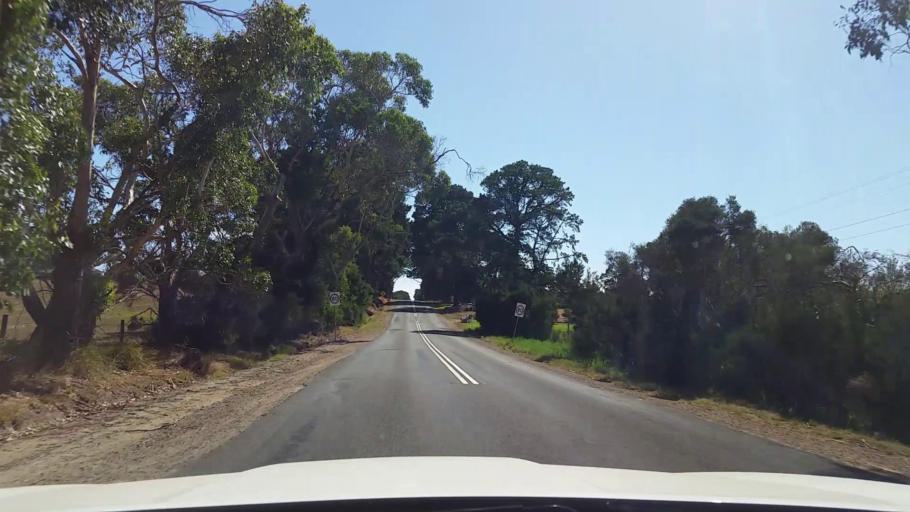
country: AU
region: Victoria
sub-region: Mornington Peninsula
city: Hastings
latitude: -38.3139
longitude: 145.1457
